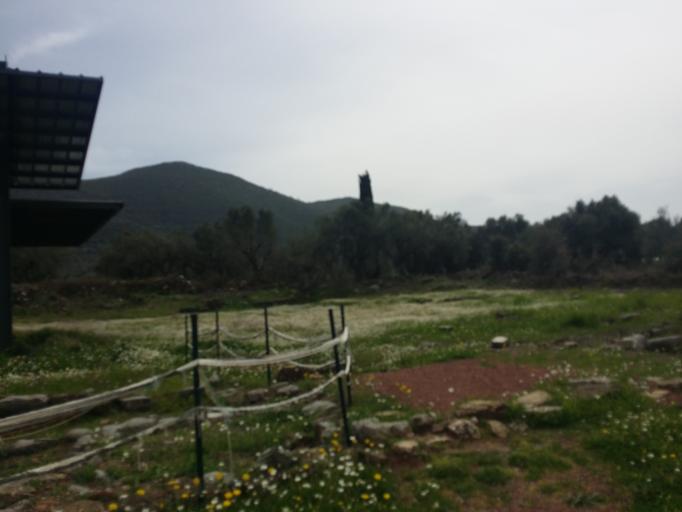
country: GR
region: Peloponnese
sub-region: Nomos Messinias
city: Meligalas
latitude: 37.1746
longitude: 21.9212
